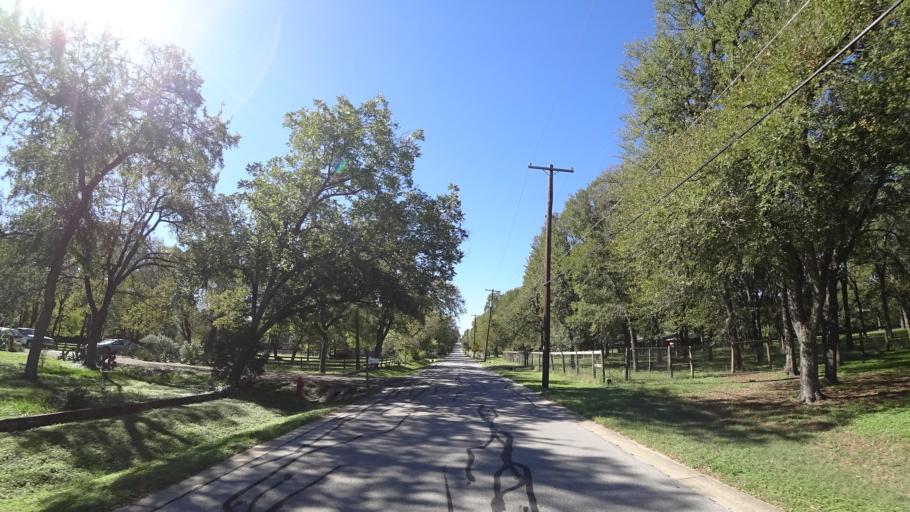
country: US
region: Texas
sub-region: Travis County
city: Rollingwood
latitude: 30.2265
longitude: -97.8086
